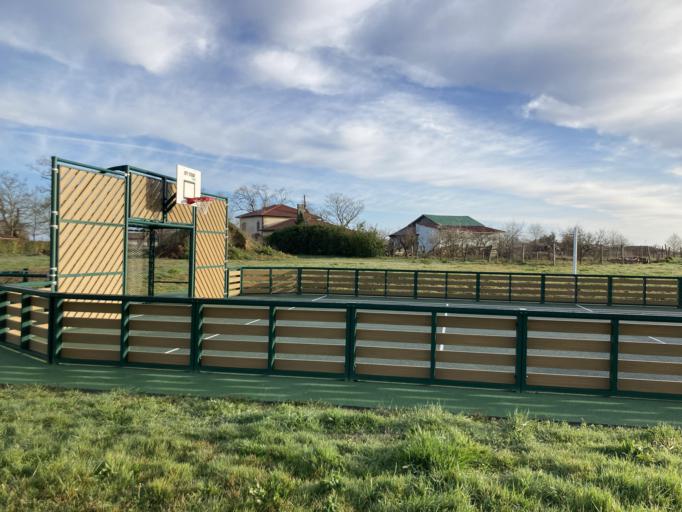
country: FR
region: Aquitaine
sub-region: Departement des Landes
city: Montfort-en-Chalosse
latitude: 43.7604
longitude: -0.8593
